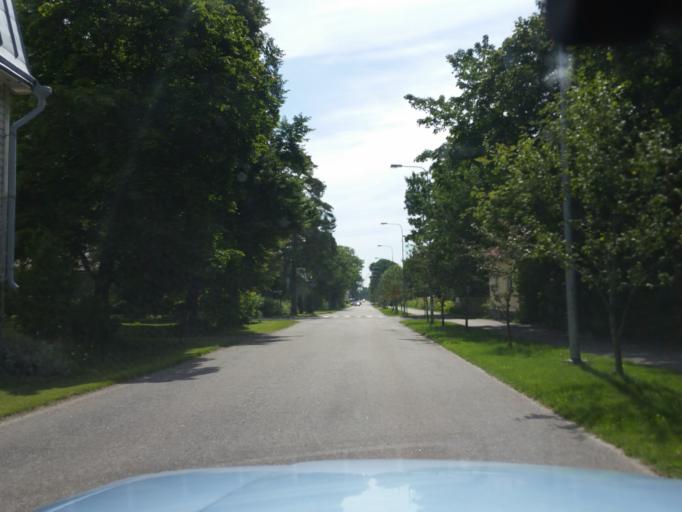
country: FI
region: Uusimaa
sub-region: Raaseporin
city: Hanko
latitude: 59.8363
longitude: 22.9437
